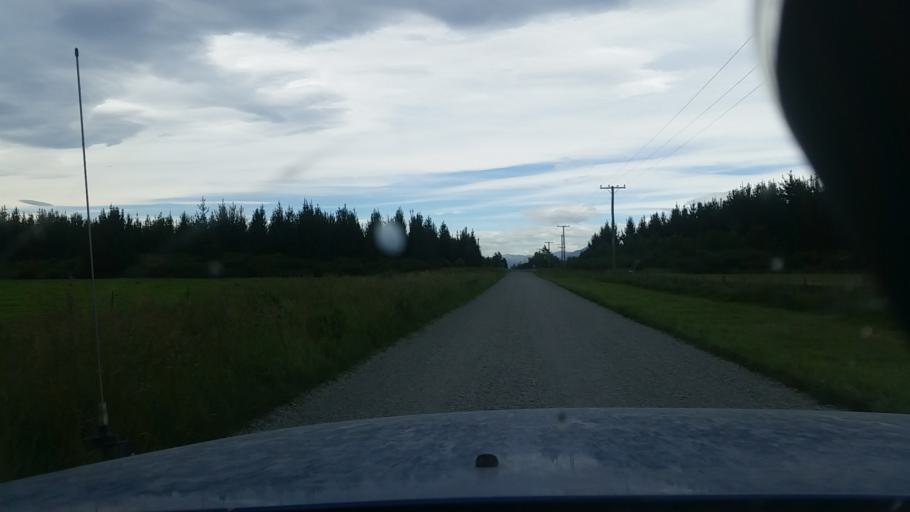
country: NZ
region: Canterbury
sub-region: Ashburton District
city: Methven
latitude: -43.7842
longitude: 171.5389
